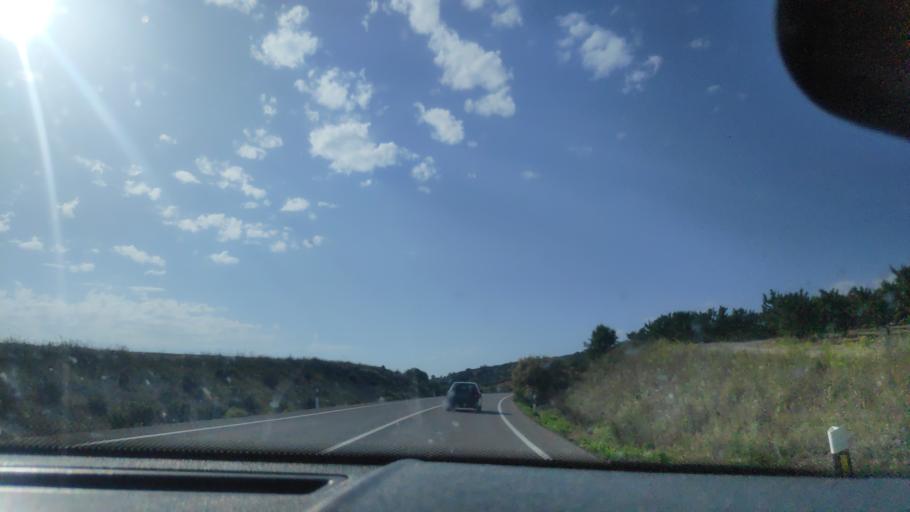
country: ES
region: Andalusia
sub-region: Provincia de Jaen
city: Frailes
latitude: 37.4411
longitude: -3.8532
